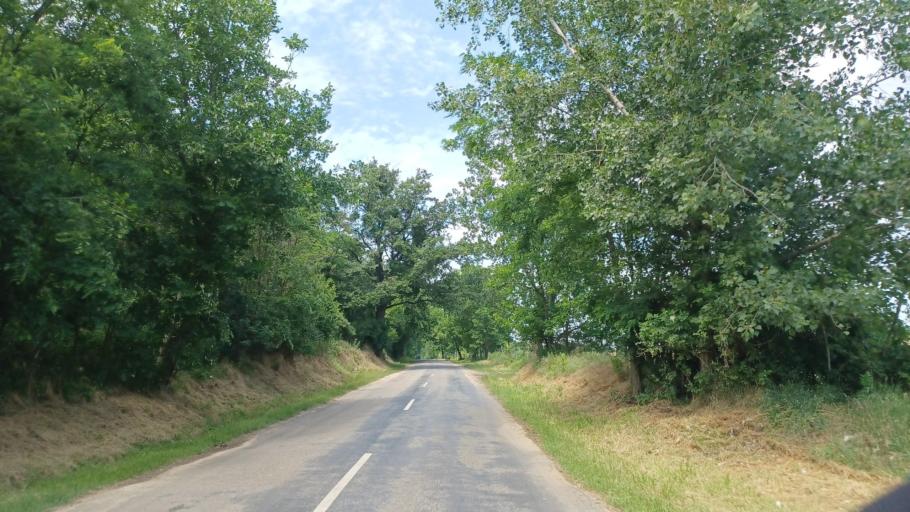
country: HU
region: Tolna
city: Simontornya
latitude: 46.7079
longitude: 18.5096
